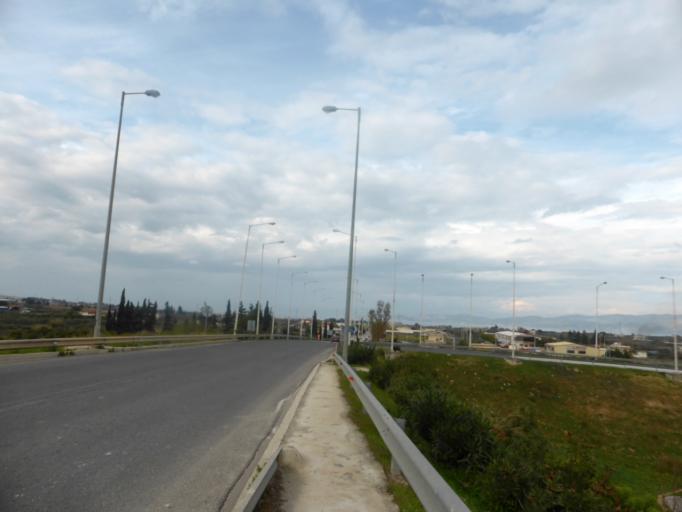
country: GR
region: Peloponnese
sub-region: Nomos Korinthias
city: Arkhaia Korinthos
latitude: 37.9152
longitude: 22.8850
